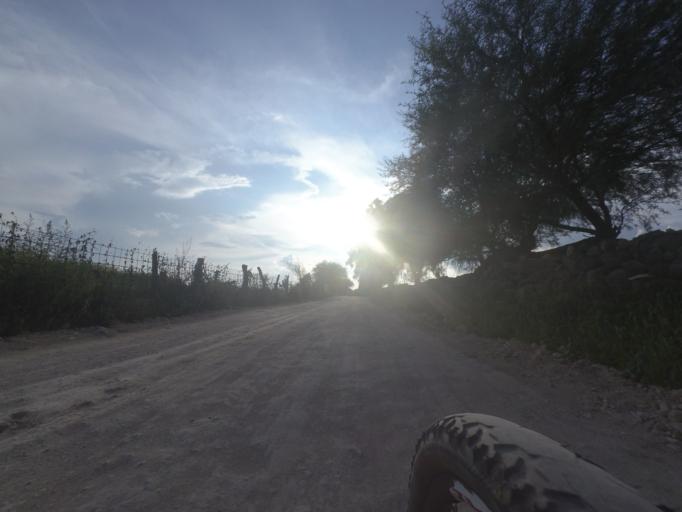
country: MX
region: Aguascalientes
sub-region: Aguascalientes
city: La Loma de los Negritos
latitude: 21.7754
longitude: -102.3663
